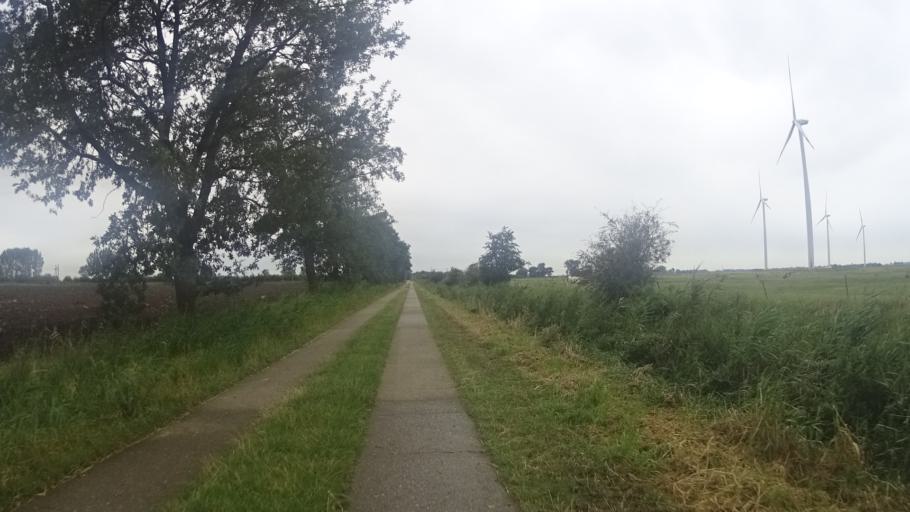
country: DE
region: Schleswig-Holstein
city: Sommerland
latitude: 53.7911
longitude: 9.5412
